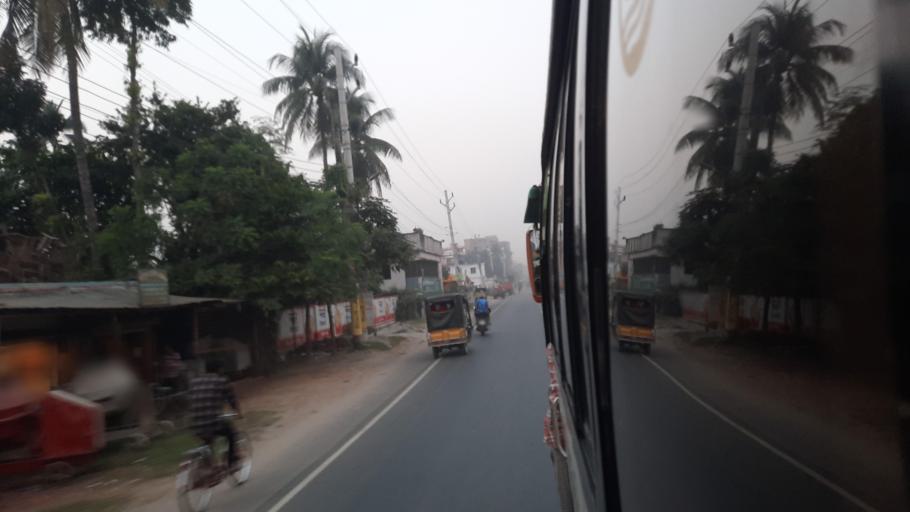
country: BD
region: Khulna
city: Jessore
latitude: 23.1733
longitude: 89.1924
